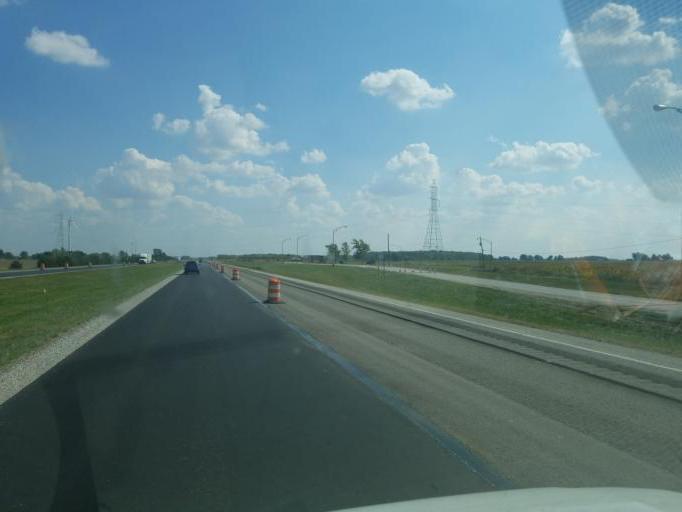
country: US
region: Ohio
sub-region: Van Wert County
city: Convoy
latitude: 40.9302
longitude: -84.6924
